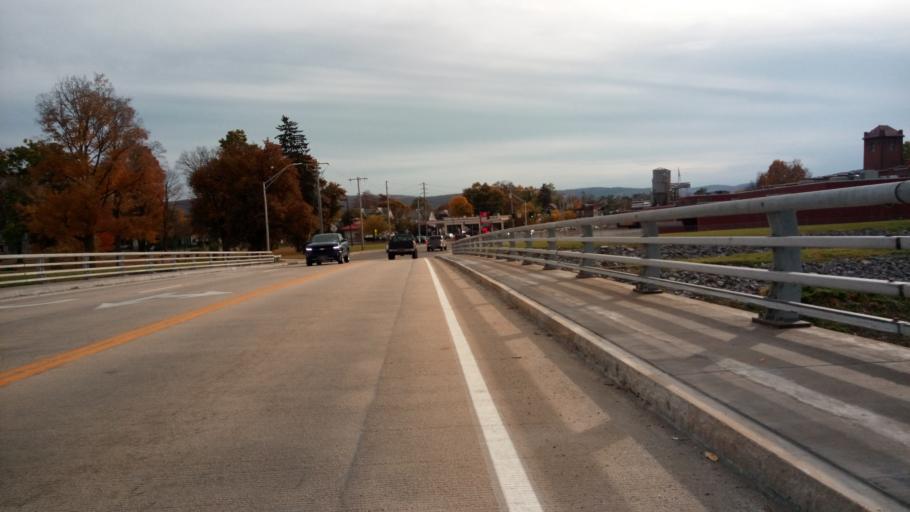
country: US
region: New York
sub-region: Chemung County
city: Elmira
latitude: 42.0872
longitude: -76.7981
